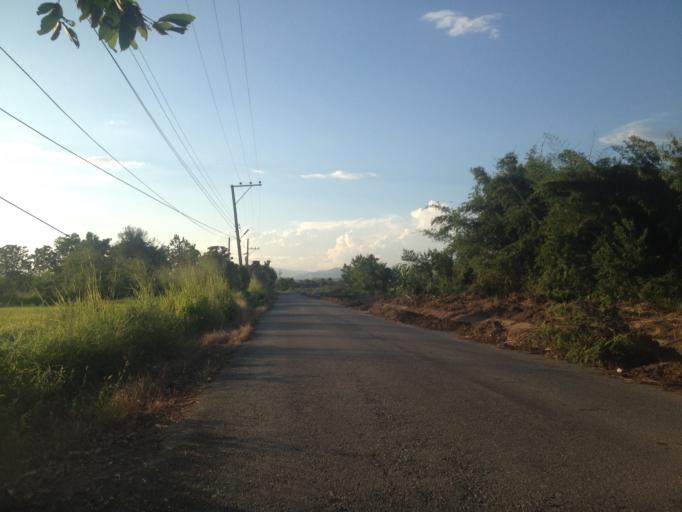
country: TH
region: Chiang Mai
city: San Pa Tong
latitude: 18.6480
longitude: 98.8939
